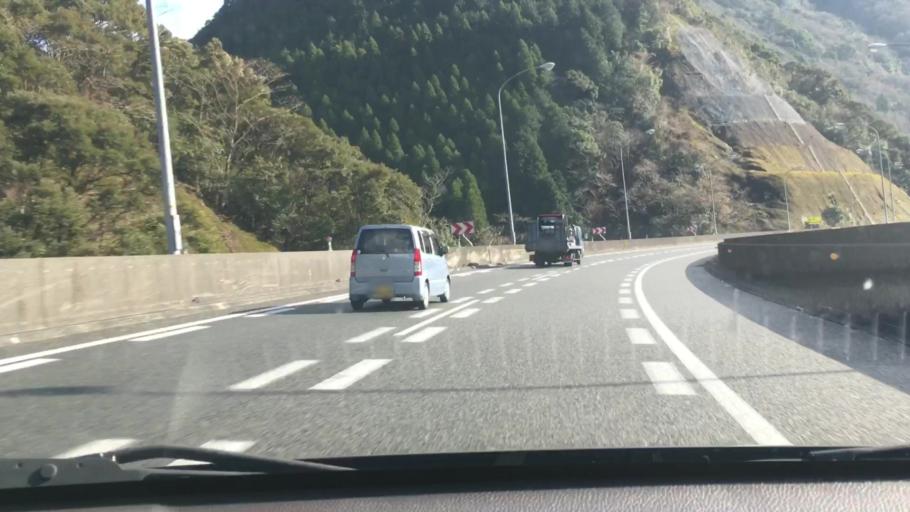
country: JP
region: Kumamoto
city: Hitoyoshi
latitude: 32.3253
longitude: 130.7580
